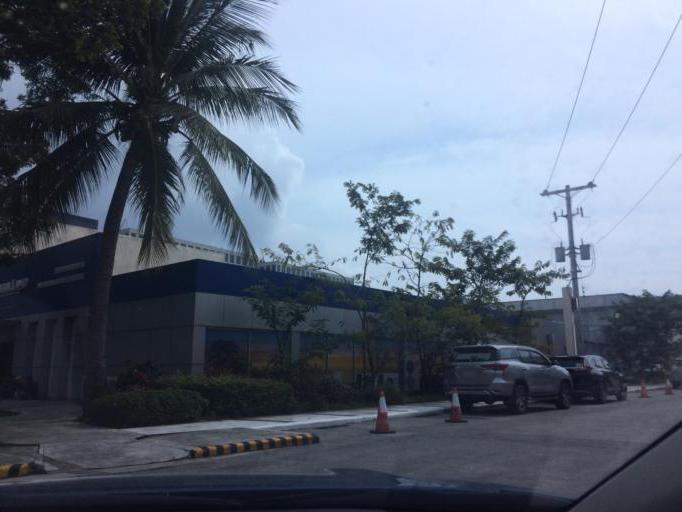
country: PH
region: Metro Manila
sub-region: Makati City
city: Makati City
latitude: 14.5377
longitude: 120.9908
